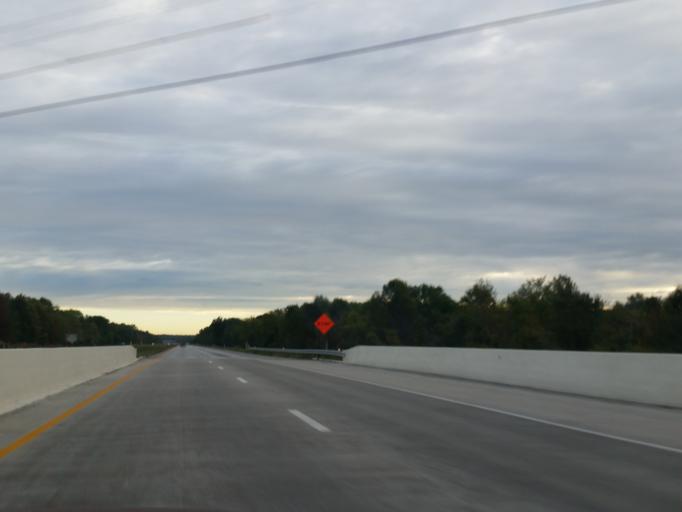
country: US
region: Ohio
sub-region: Ashtabula County
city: Ashtabula
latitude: 41.7985
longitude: -80.8348
